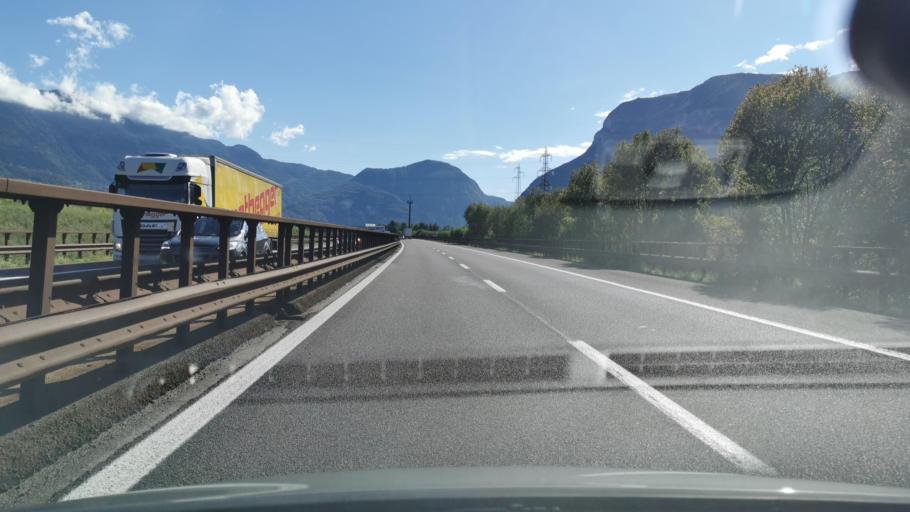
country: IT
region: Trentino-Alto Adige
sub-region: Bolzano
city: Laghetti
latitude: 46.2933
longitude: 11.2396
